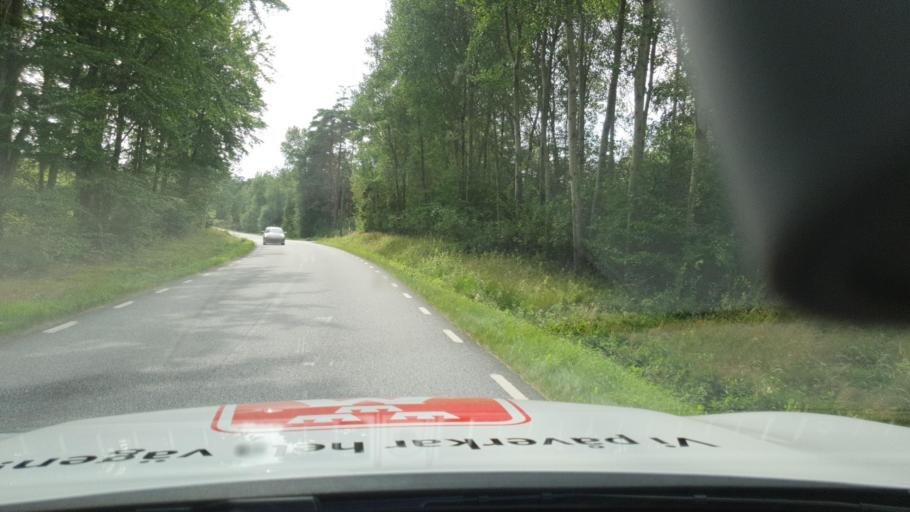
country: SE
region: Vaestra Goetaland
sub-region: Sotenas Kommun
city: Hunnebostrand
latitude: 58.5637
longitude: 11.2854
